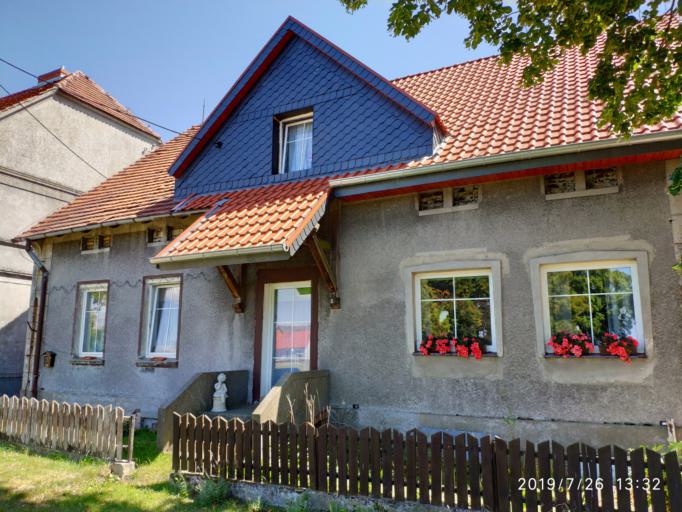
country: PL
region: Lubusz
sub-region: Powiat swiebodzinski
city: Lagow
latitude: 52.3518
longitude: 15.2690
